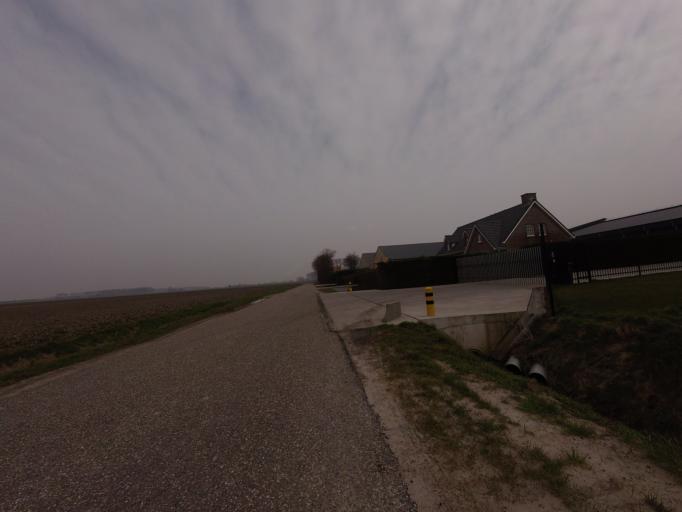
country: BE
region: Flanders
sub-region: Provincie Oost-Vlaanderen
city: Sint-Gillis-Waas
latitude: 51.3218
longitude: 4.1659
